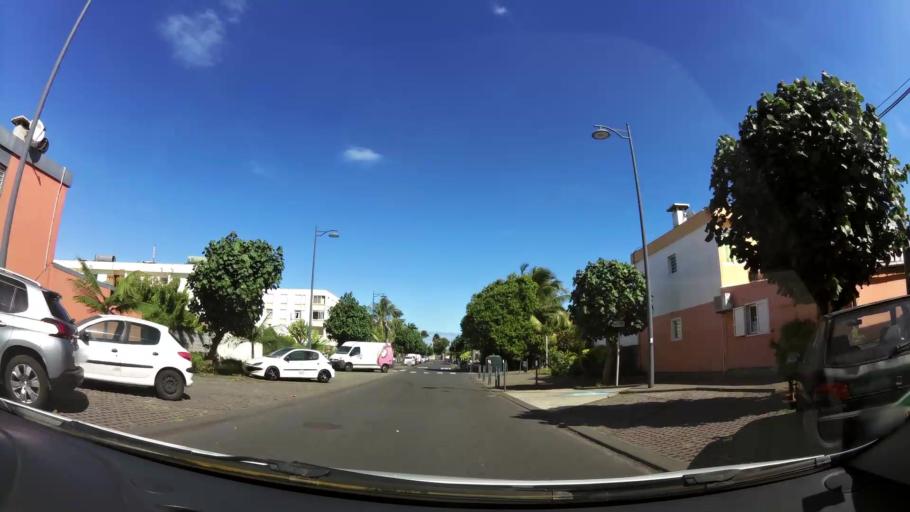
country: RE
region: Reunion
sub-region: Reunion
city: Saint-Pierre
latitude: -21.3397
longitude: 55.4633
